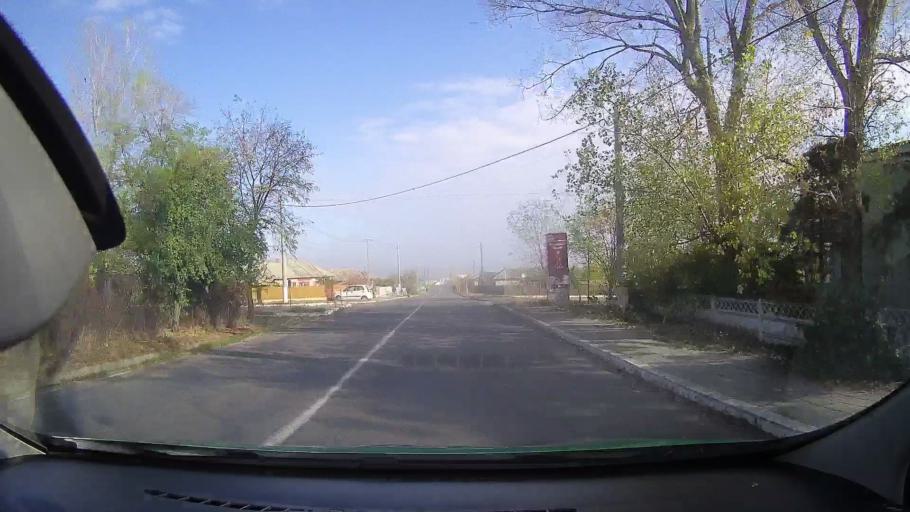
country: RO
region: Tulcea
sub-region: Comuna Mahmudia
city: Mahmudia
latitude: 45.0824
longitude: 29.0821
